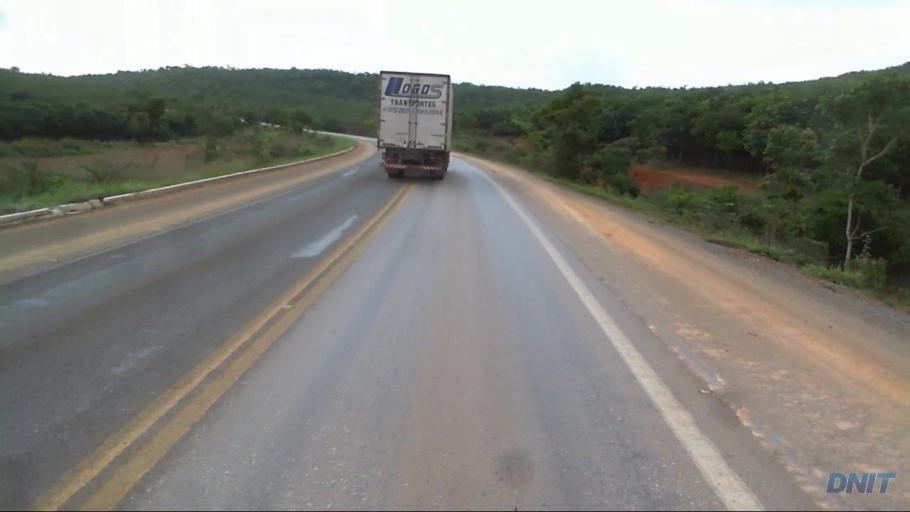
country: BR
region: Goias
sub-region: Barro Alto
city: Barro Alto
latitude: -14.9316
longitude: -48.9491
